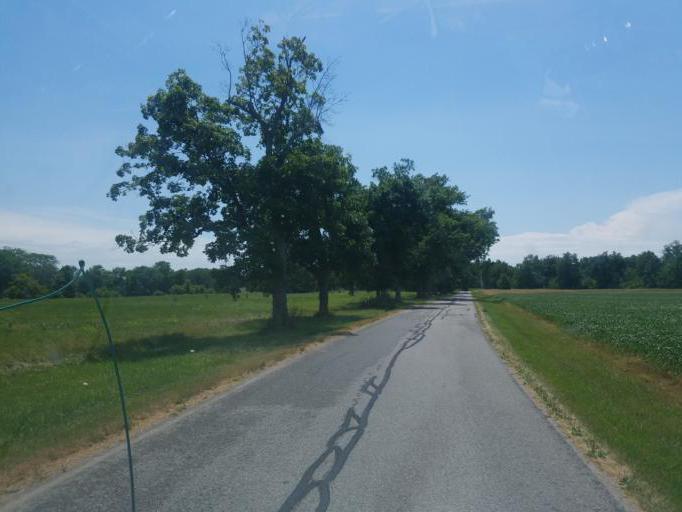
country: US
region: Ohio
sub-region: Paulding County
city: Antwerp
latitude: 41.1777
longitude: -84.7911
